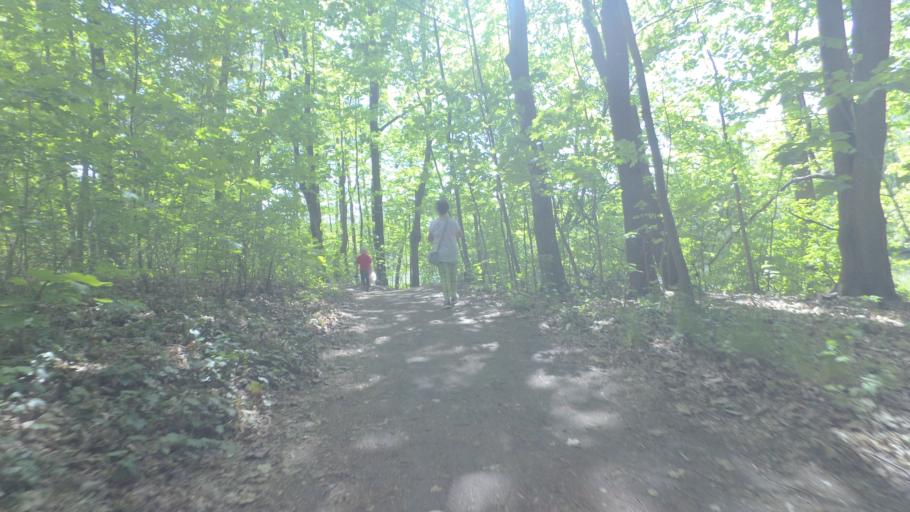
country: DE
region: Brandenburg
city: Erkner
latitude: 52.4283
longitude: 13.7641
